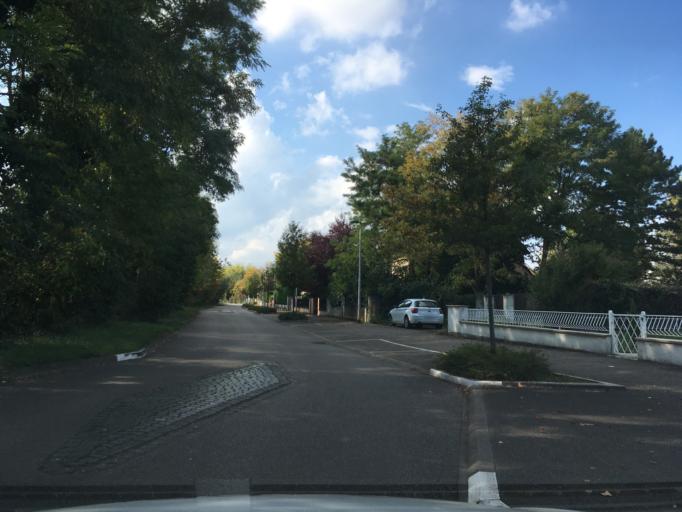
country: FR
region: Alsace
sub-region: Departement du Haut-Rhin
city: Colmar
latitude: 48.0591
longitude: 7.3486
